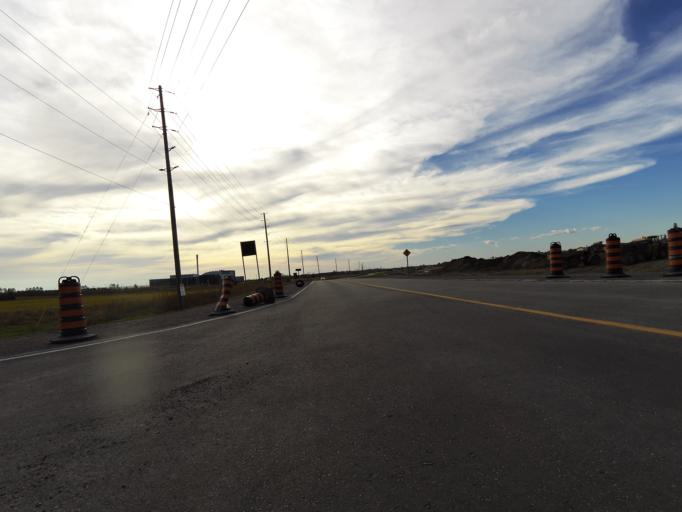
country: CA
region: Ontario
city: Oshawa
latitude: 43.8800
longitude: -78.7426
